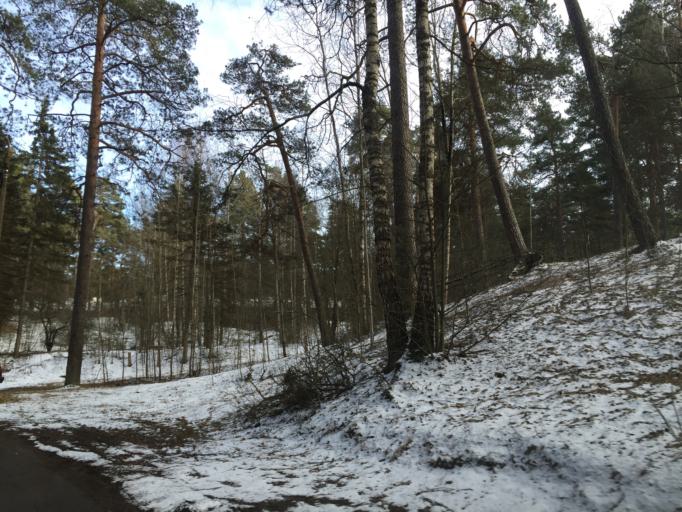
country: LV
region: Riga
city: Jaunciems
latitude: 56.9837
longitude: 24.2132
